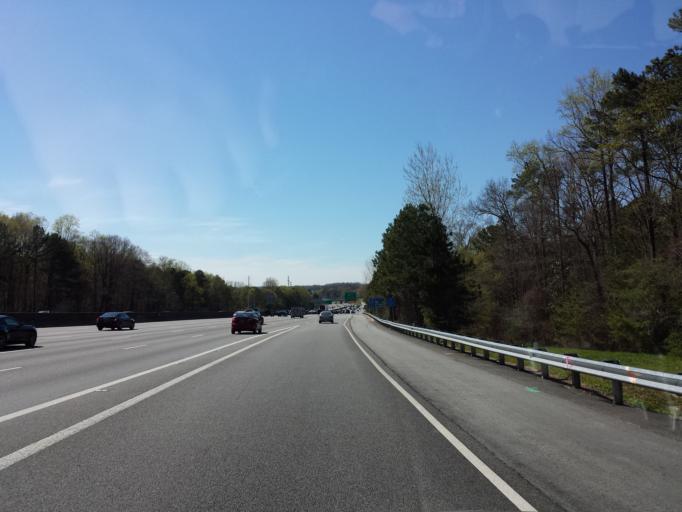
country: US
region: Georgia
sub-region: Fulton County
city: Sandy Springs
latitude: 33.9105
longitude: -84.3656
